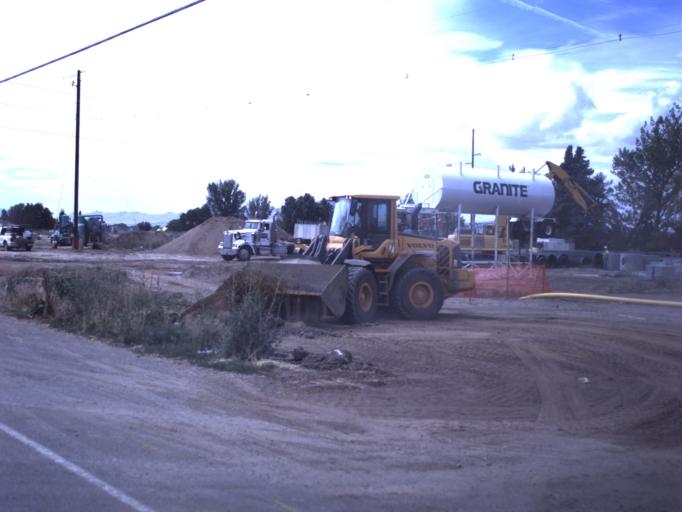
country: US
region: Utah
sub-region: Davis County
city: West Point
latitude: 41.1120
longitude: -112.0646
